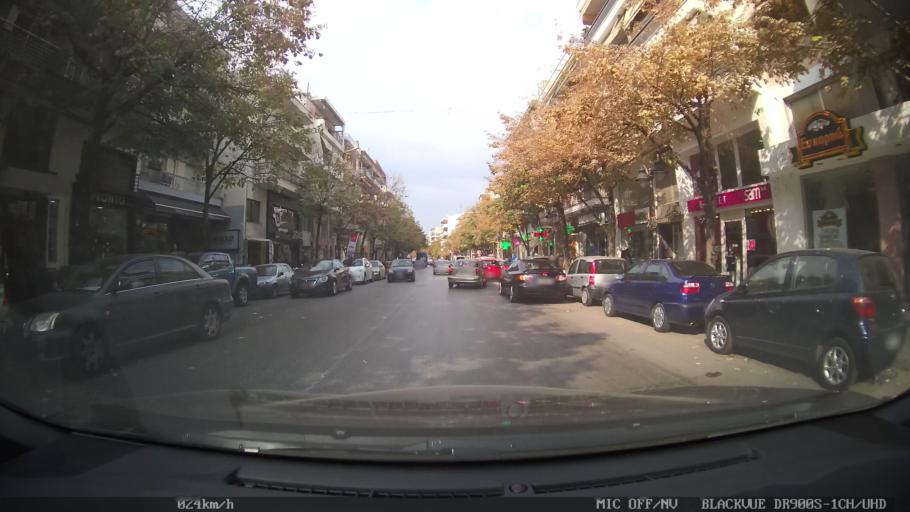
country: GR
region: Central Macedonia
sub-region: Nomos Thessalonikis
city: Triandria
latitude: 40.6135
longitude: 22.9807
